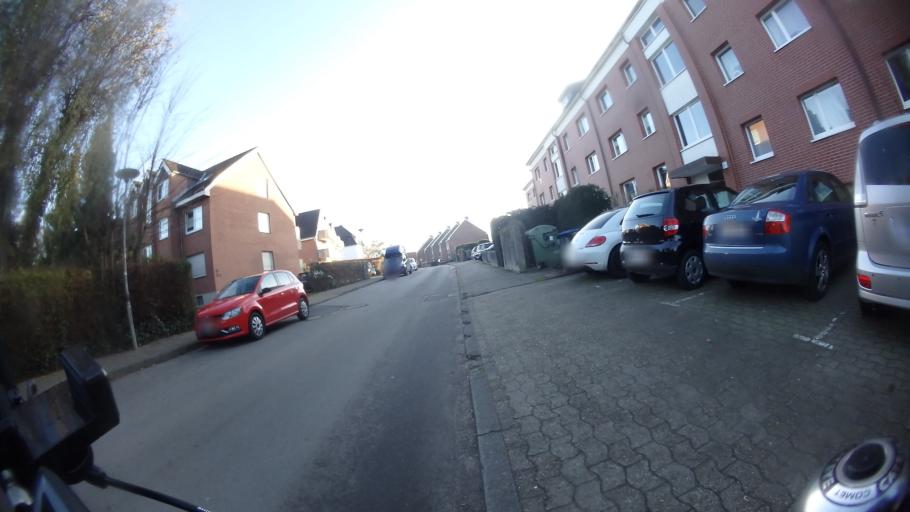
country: DE
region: Schleswig-Holstein
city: Travemuende
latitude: 53.9618
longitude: 10.8656
